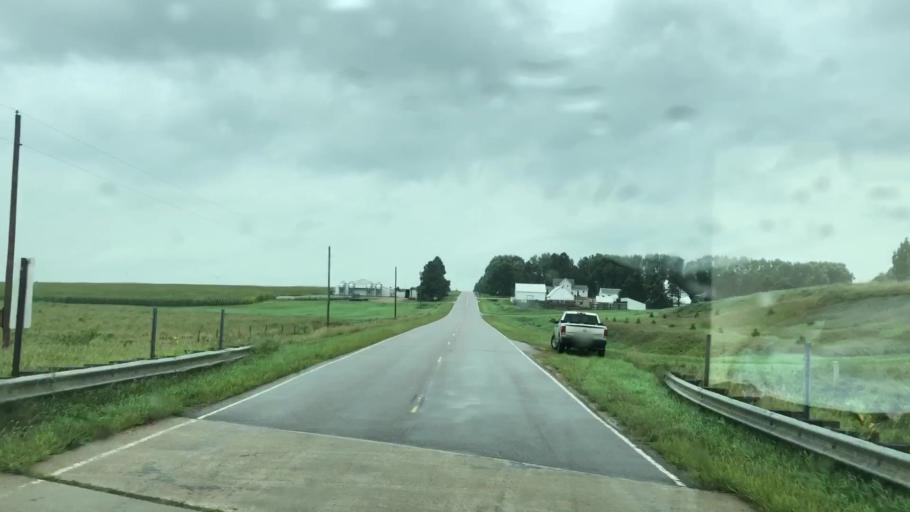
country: US
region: Iowa
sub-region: O'Brien County
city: Sanborn
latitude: 43.2404
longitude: -95.7235
